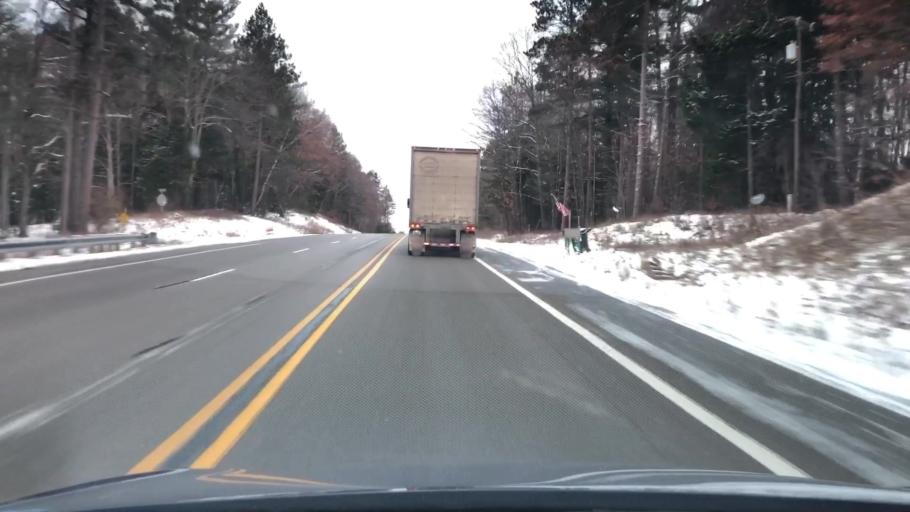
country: US
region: Michigan
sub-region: Wexford County
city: Cadillac
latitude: 44.1865
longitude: -85.3881
